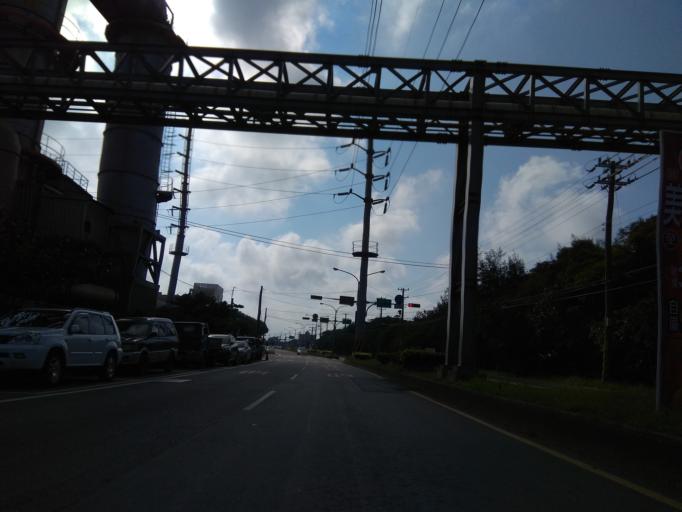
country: TW
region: Taiwan
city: Taoyuan City
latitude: 25.0440
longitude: 121.1074
